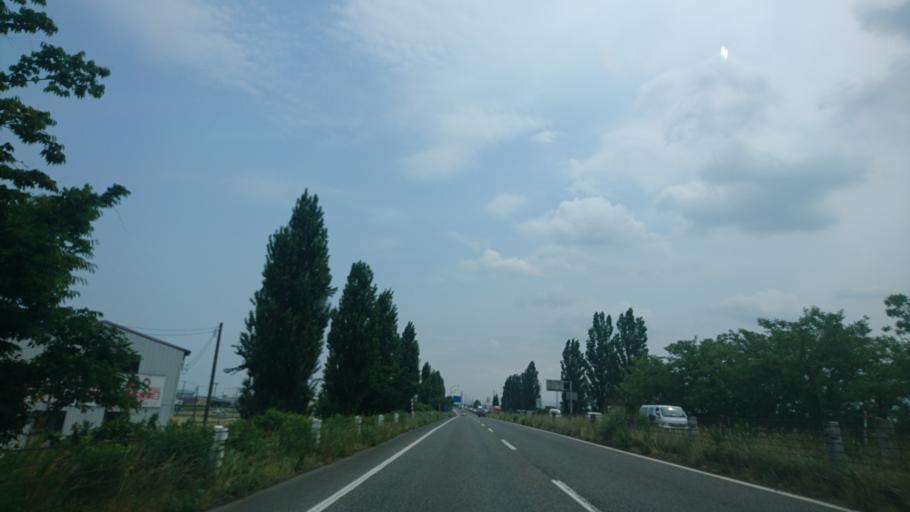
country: JP
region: Niigata
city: Kameda-honcho
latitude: 37.9394
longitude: 139.1769
